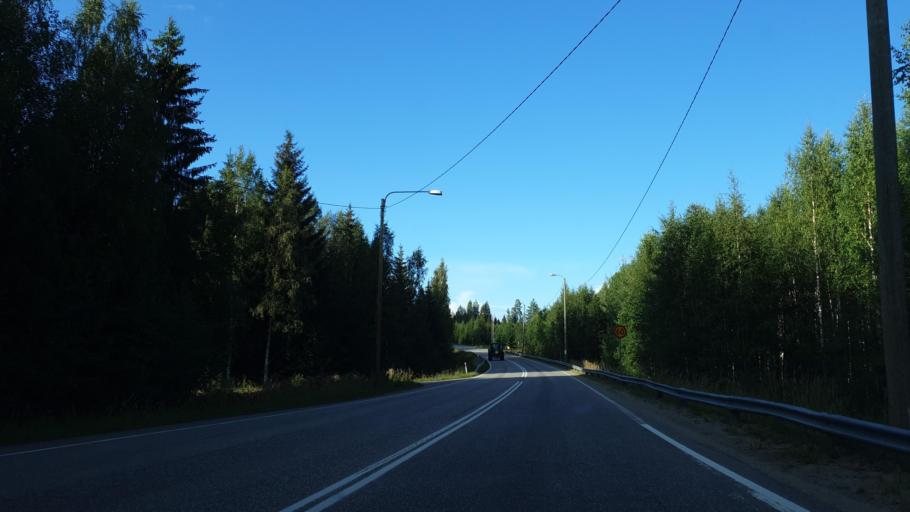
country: FI
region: Northern Savo
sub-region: Koillis-Savo
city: Kaavi
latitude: 62.9790
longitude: 28.4489
